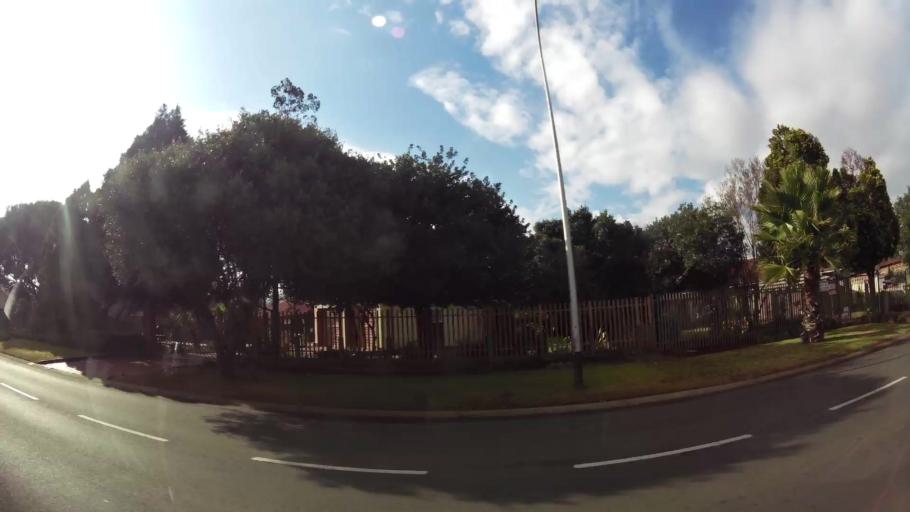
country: ZA
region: Gauteng
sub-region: Sedibeng District Municipality
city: Meyerton
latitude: -26.5534
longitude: 28.0324
